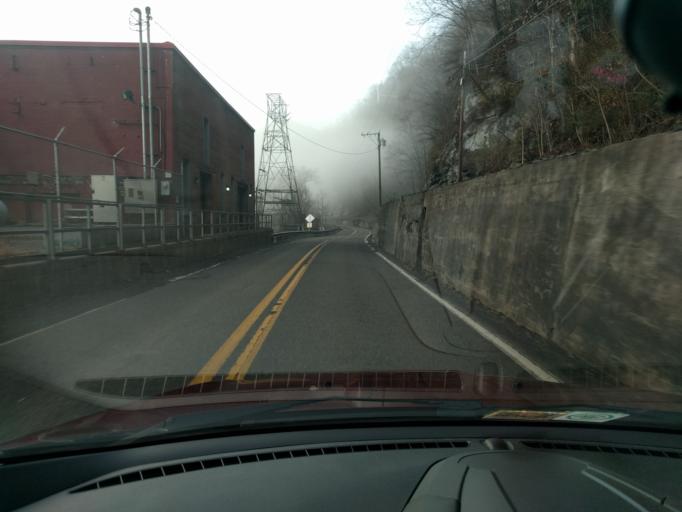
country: US
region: West Virginia
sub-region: Fayette County
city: Ansted
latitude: 38.1482
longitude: -81.2148
